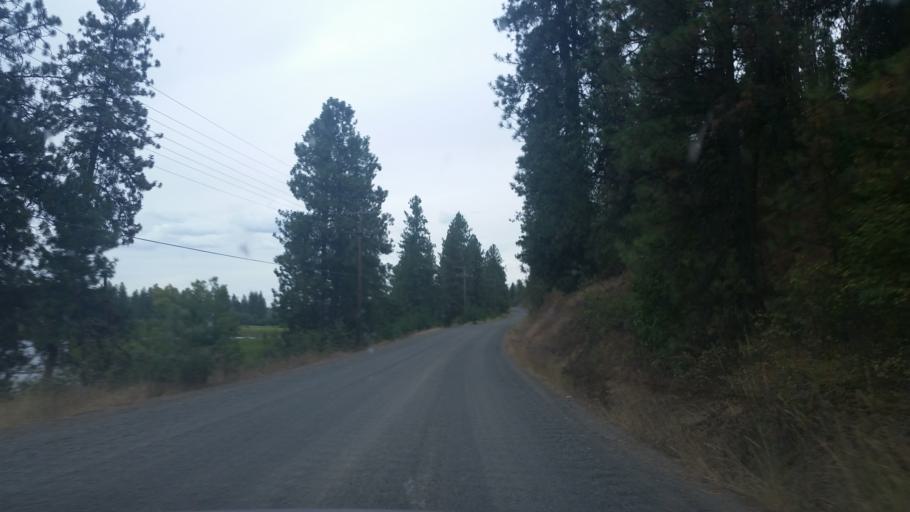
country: US
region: Washington
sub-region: Spokane County
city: Cheney
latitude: 47.5477
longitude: -117.5970
